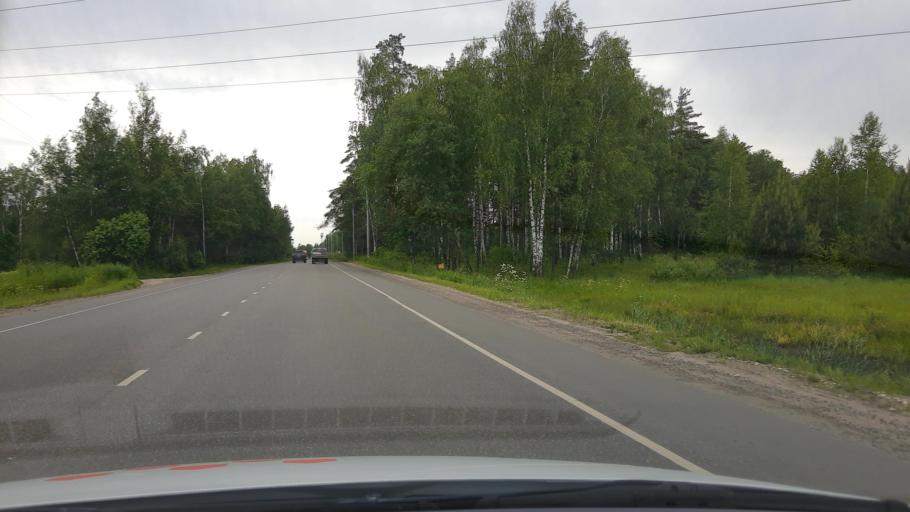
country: RU
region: Moskovskaya
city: Noginsk
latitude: 55.8613
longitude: 38.4112
